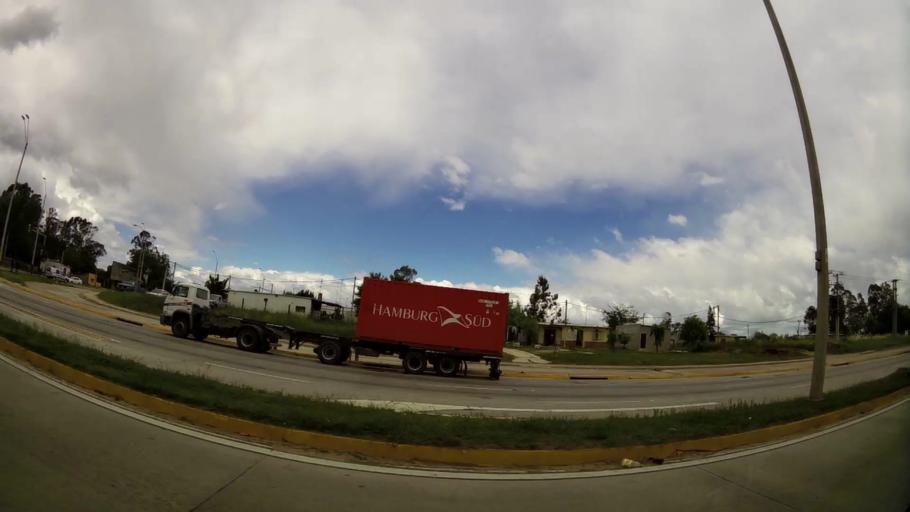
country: UY
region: Canelones
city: Toledo
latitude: -34.7957
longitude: -56.1372
